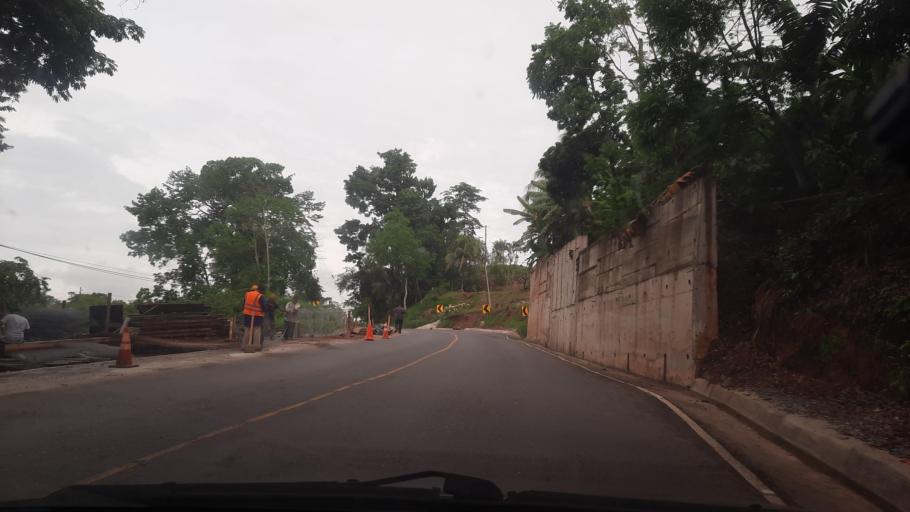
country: GT
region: Izabal
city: Morales
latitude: 15.5058
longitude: -88.8110
